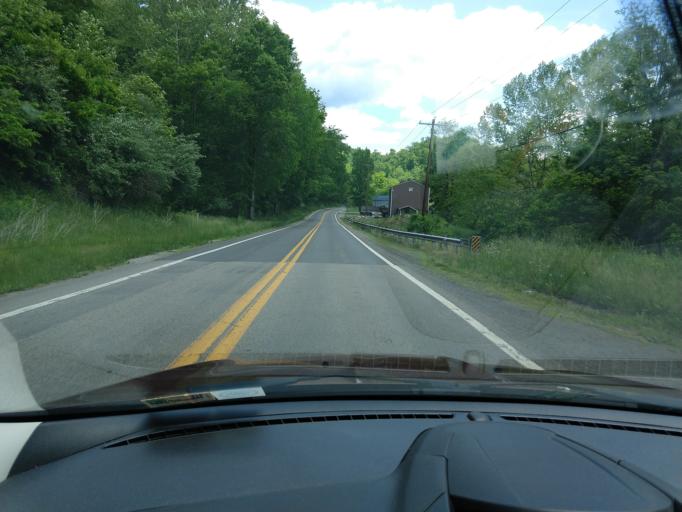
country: US
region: West Virginia
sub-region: Gilmer County
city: Glenville
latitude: 38.9304
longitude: -80.7822
